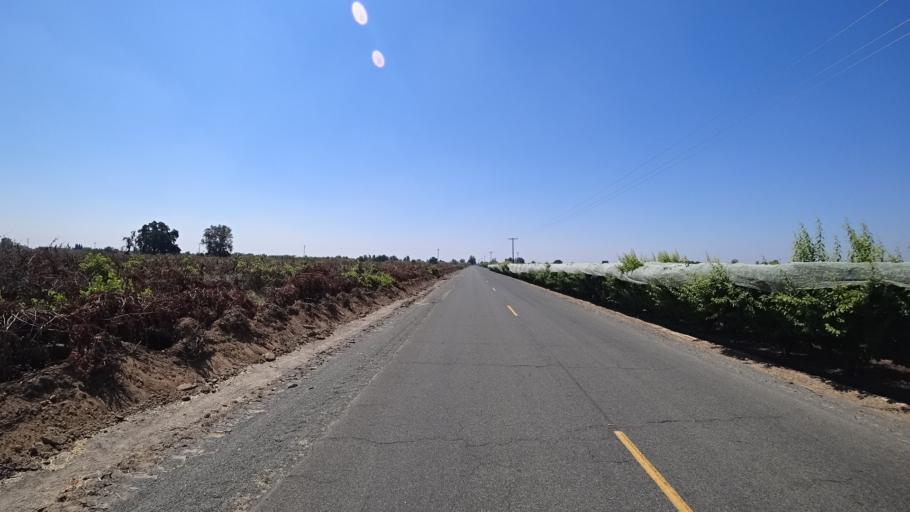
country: US
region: California
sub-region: Fresno County
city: Kingsburg
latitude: 36.4650
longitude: -119.6002
